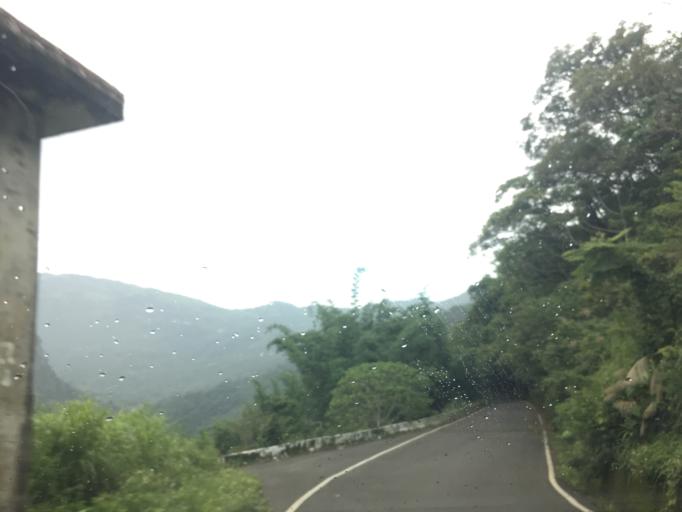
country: TW
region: Taiwan
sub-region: Yunlin
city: Douliu
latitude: 23.5729
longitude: 120.6425
